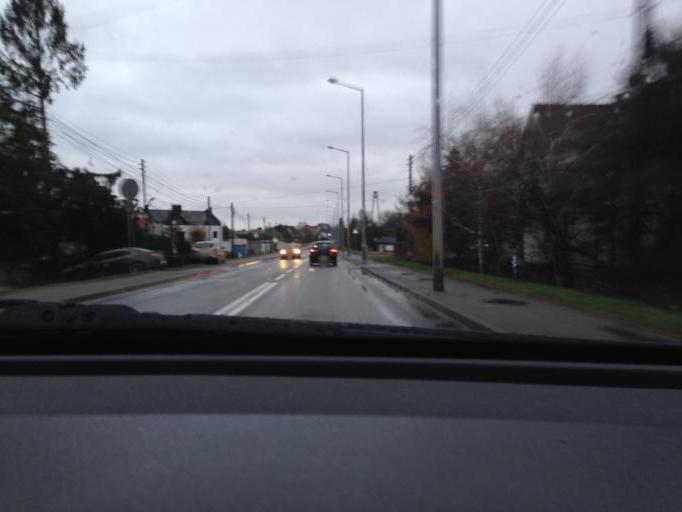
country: PL
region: Opole Voivodeship
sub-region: Powiat opolski
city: Opole
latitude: 50.6949
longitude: 17.9557
